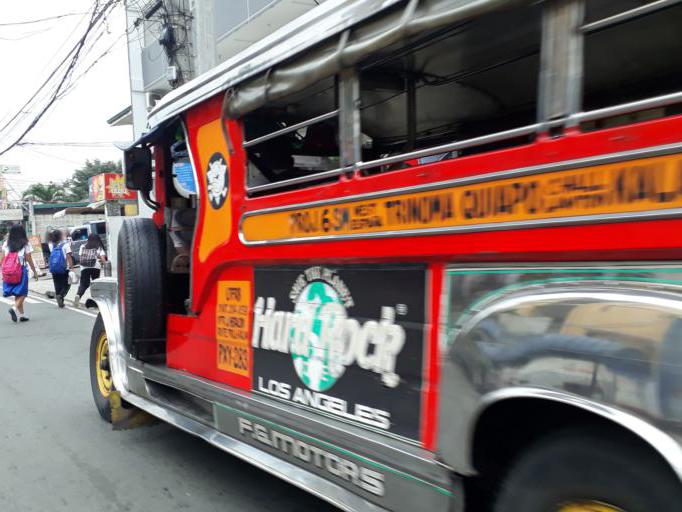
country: PH
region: Calabarzon
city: Bagong Pagasa
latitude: 14.6642
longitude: 121.0378
